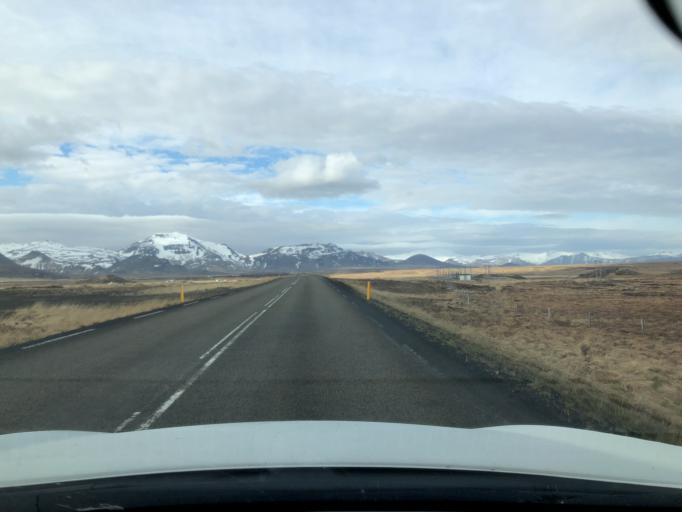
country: IS
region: West
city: Stykkisholmur
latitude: 65.0203
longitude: -22.7538
